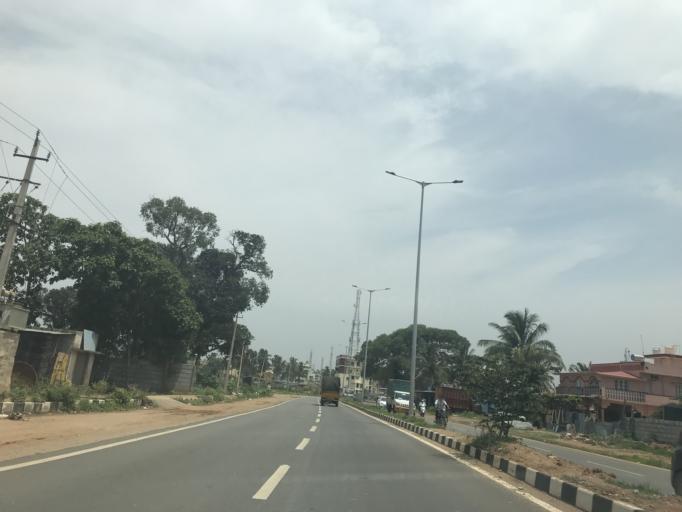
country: IN
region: Karnataka
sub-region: Bangalore Urban
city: Yelahanka
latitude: 13.1384
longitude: 77.6701
